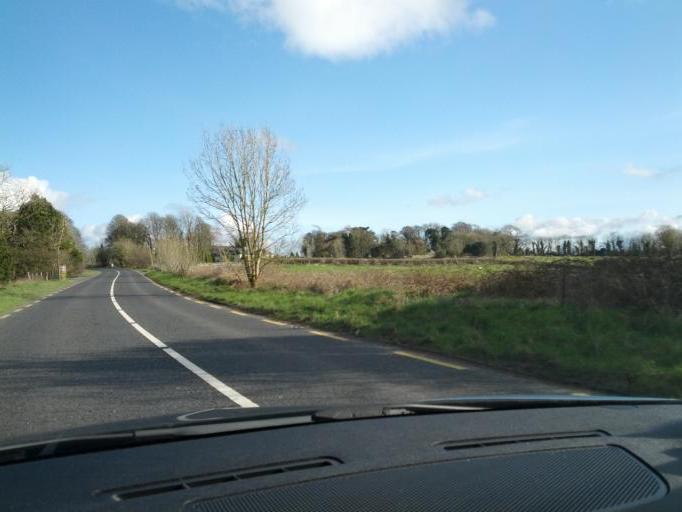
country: IE
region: Connaught
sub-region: Roscommon
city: Roscommon
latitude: 53.6575
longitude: -8.2636
